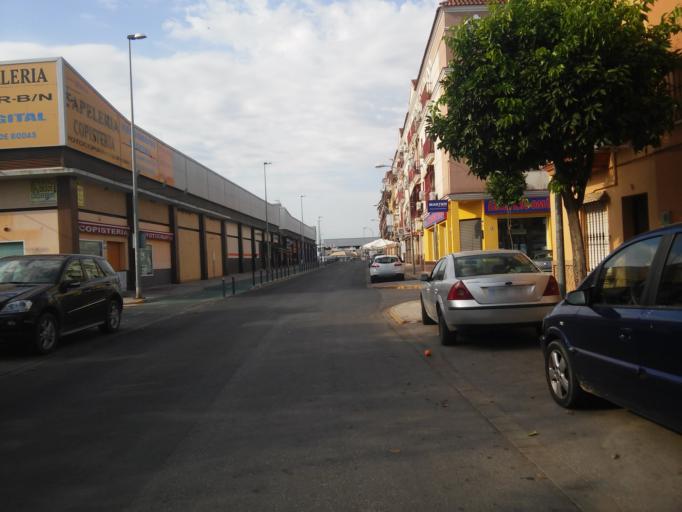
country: ES
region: Andalusia
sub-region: Provincia de Sevilla
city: La Rinconada
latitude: 37.4884
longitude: -5.9477
